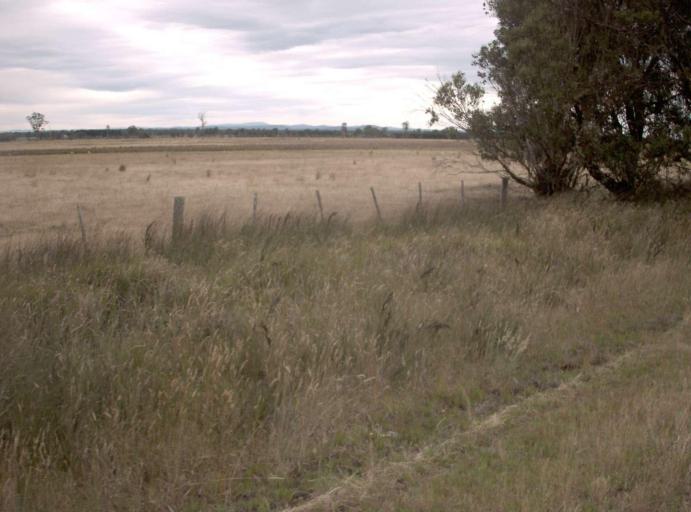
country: AU
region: Victoria
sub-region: East Gippsland
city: Bairnsdale
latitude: -37.9615
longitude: 147.4949
